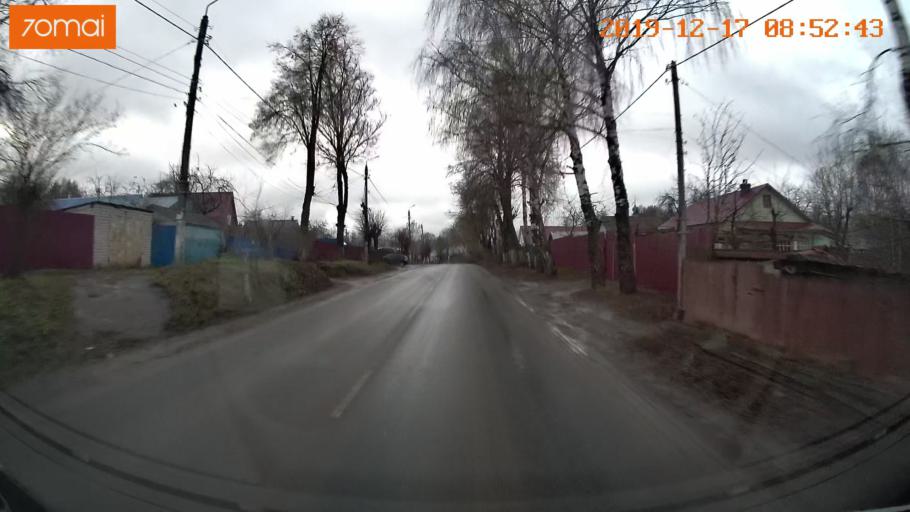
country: RU
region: Vladimir
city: Kosterevo
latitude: 55.9462
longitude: 39.6320
